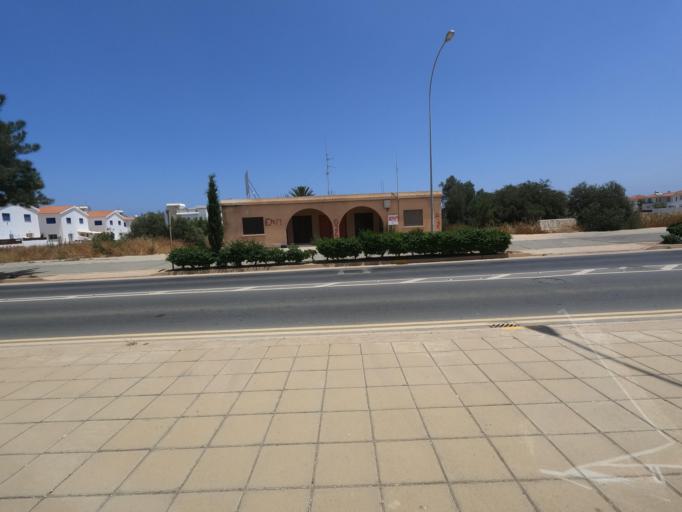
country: CY
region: Ammochostos
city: Protaras
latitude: 35.0329
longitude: 34.0275
